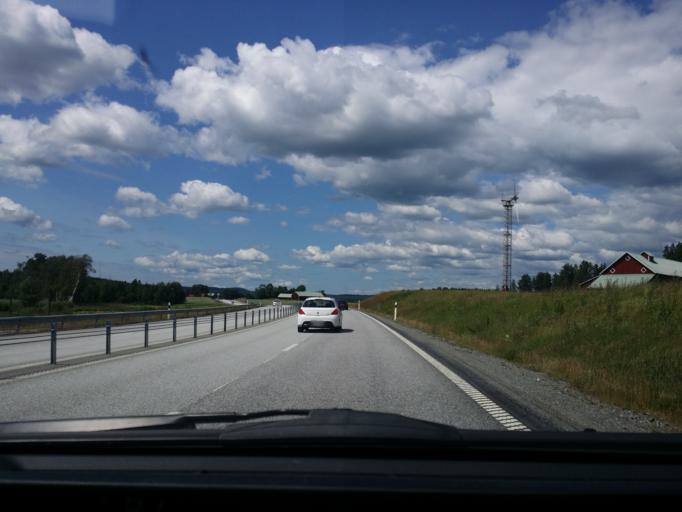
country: SE
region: OErebro
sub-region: Orebro Kommun
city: Hovsta
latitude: 59.3980
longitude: 15.2010
